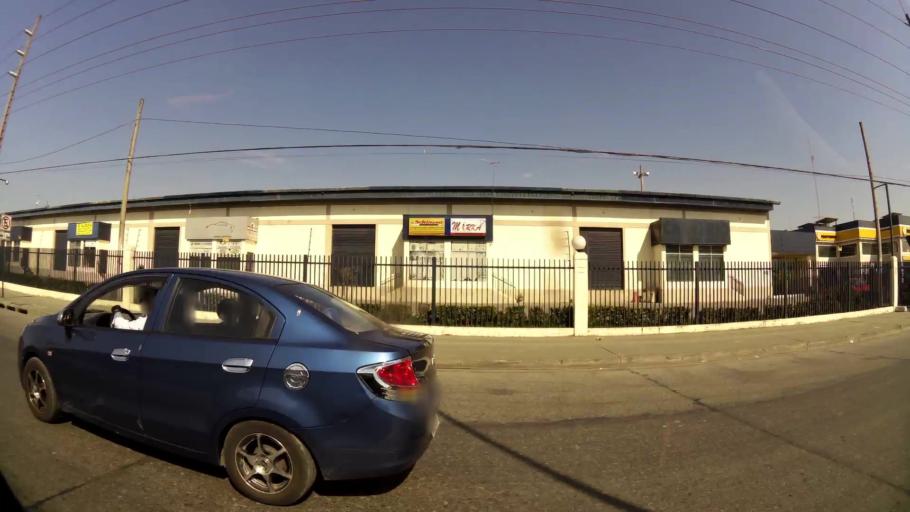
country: EC
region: Guayas
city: Santa Lucia
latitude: -2.1009
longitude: -79.9353
